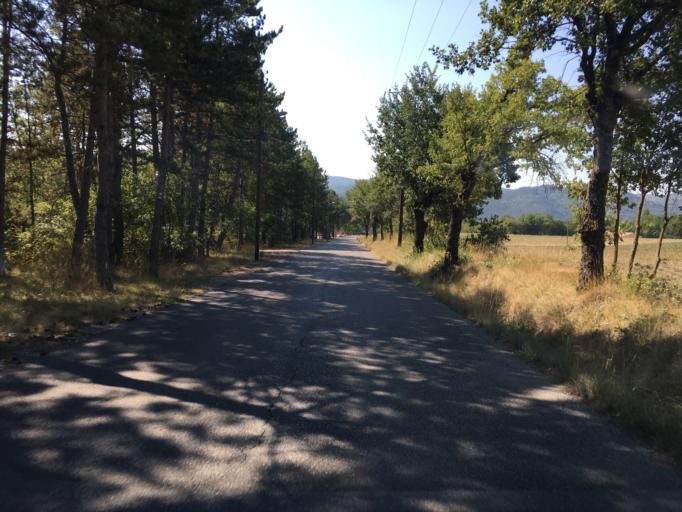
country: FR
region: Provence-Alpes-Cote d'Azur
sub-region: Departement des Alpes-de-Haute-Provence
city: Mallemoisson
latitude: 44.0541
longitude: 6.1487
